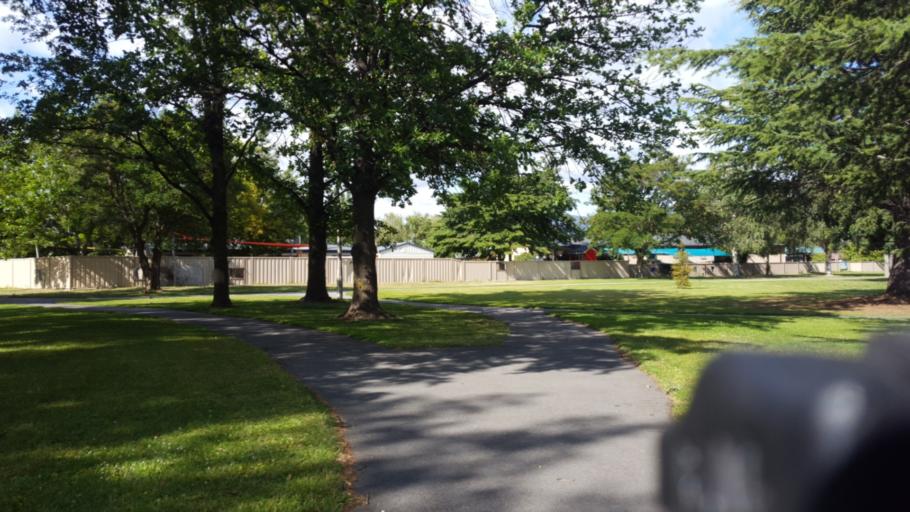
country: NZ
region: Otago
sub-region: Queenstown-Lakes District
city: Wanaka
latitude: -45.0421
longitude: 169.1869
